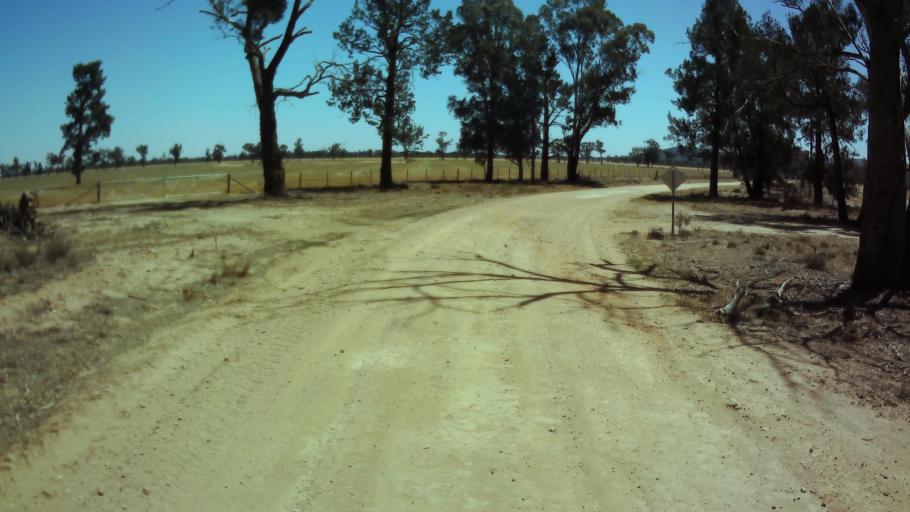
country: AU
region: New South Wales
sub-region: Weddin
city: Grenfell
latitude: -34.0269
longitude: 147.9618
